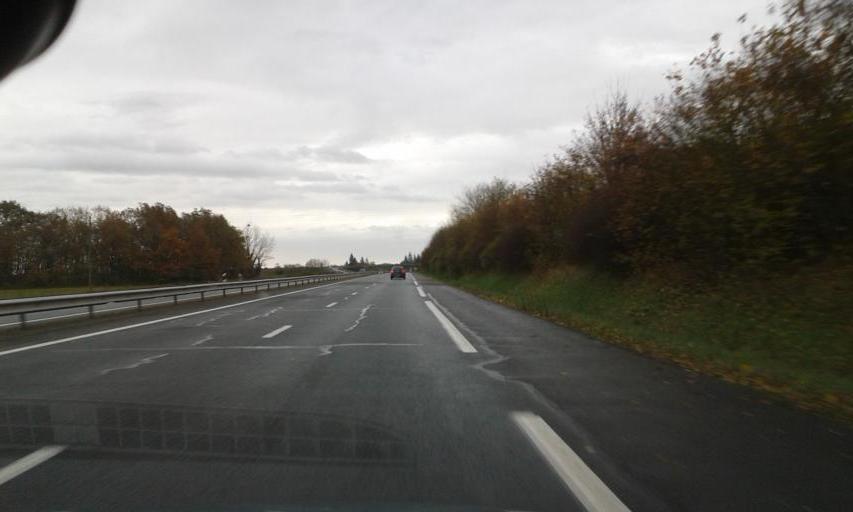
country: FR
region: Centre
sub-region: Departement du Loiret
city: Chateauneuf-sur-Loire
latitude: 47.8935
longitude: 2.2136
